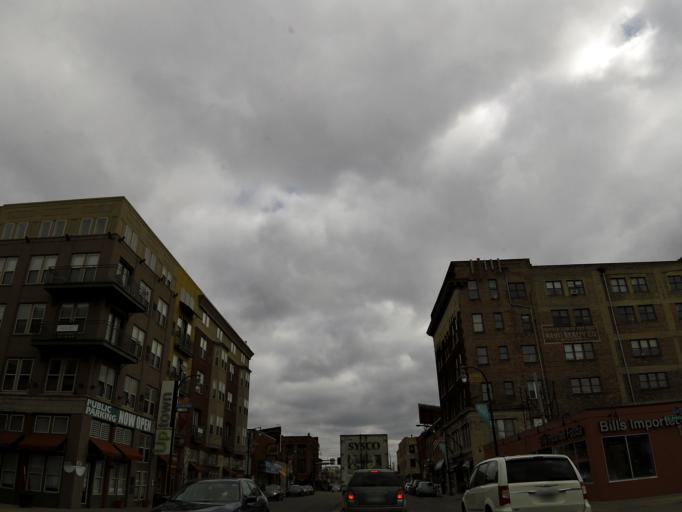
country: US
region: Minnesota
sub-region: Hennepin County
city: Minneapolis
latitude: 44.9484
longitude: -93.2896
